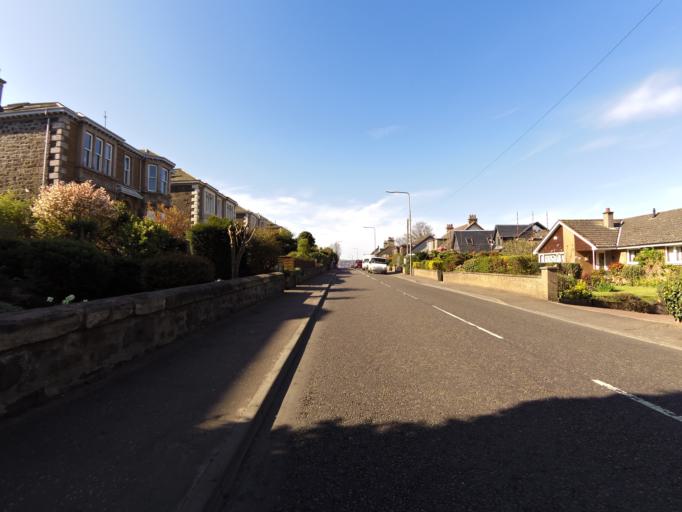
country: GB
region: Scotland
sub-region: Fife
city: Newport-On-Tay
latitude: 56.4447
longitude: -2.9375
